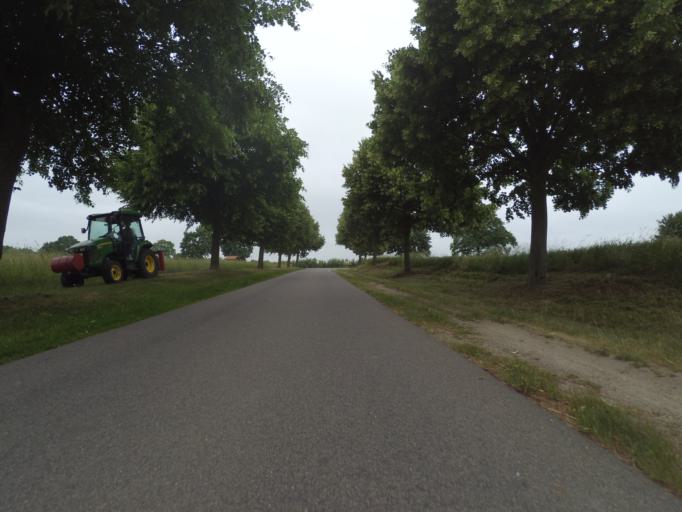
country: DE
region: Mecklenburg-Vorpommern
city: Dobbertin
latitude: 53.5830
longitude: 12.0196
